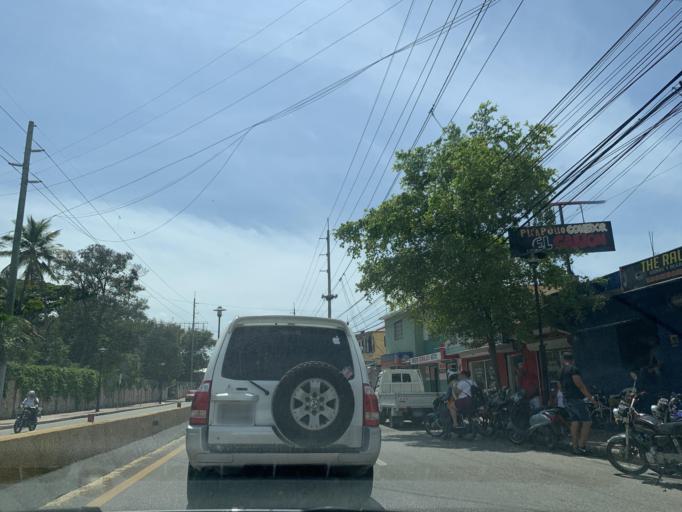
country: DO
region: Puerto Plata
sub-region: Puerto Plata
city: Puerto Plata
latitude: 19.7923
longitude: -70.7062
